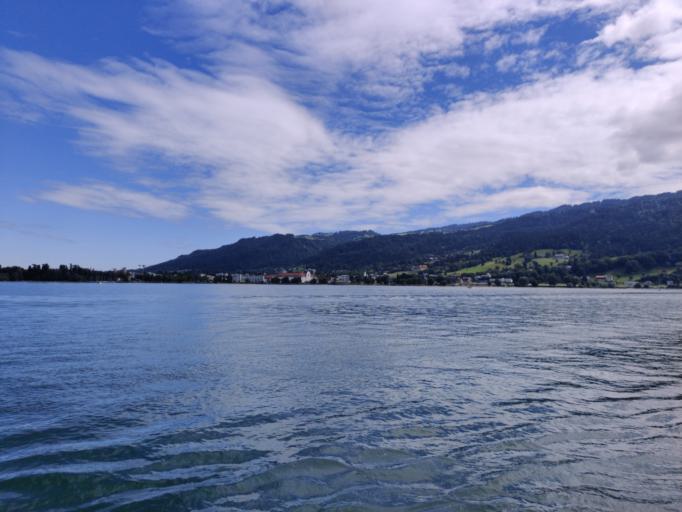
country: AT
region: Vorarlberg
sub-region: Politischer Bezirk Bregenz
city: Lochau
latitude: 47.5201
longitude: 9.7339
